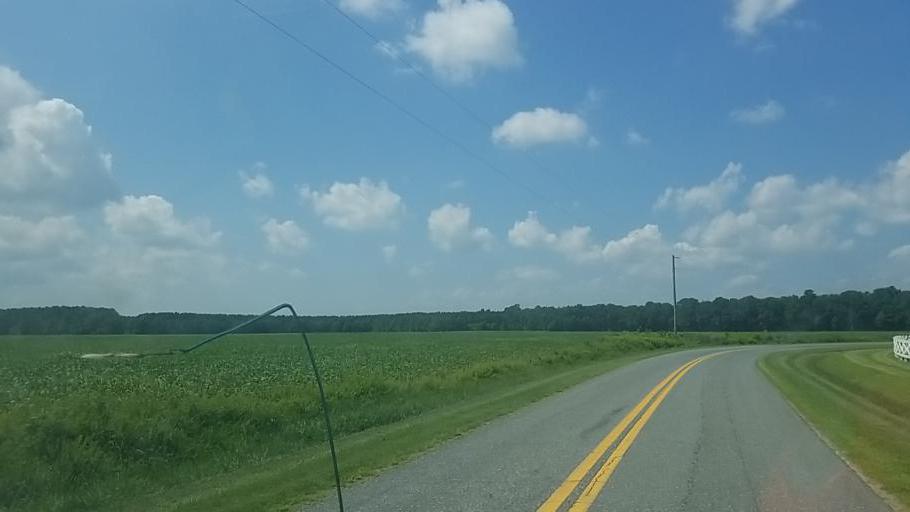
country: US
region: Maryland
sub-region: Wicomico County
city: Hebron
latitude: 38.4479
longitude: -75.8489
